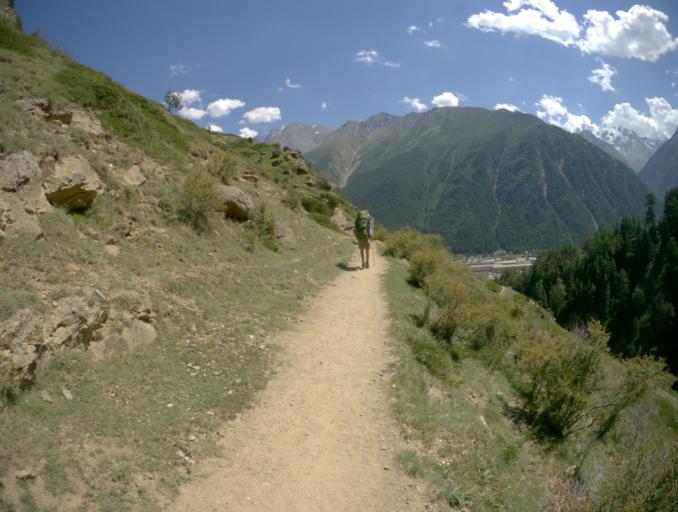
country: RU
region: Kabardino-Balkariya
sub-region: El'brusskiy Rayon
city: El'brus
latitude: 43.2633
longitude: 42.6375
